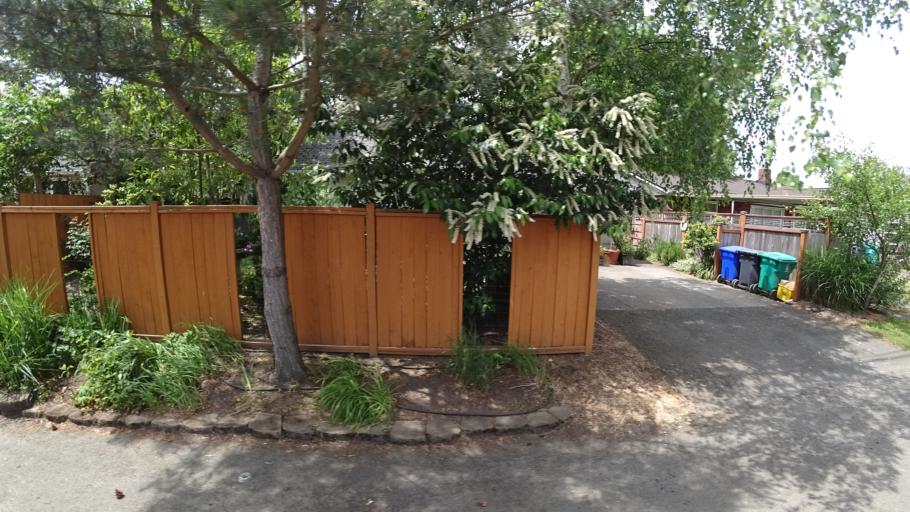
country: US
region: Oregon
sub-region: Multnomah County
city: Lents
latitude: 45.4681
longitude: -122.5923
